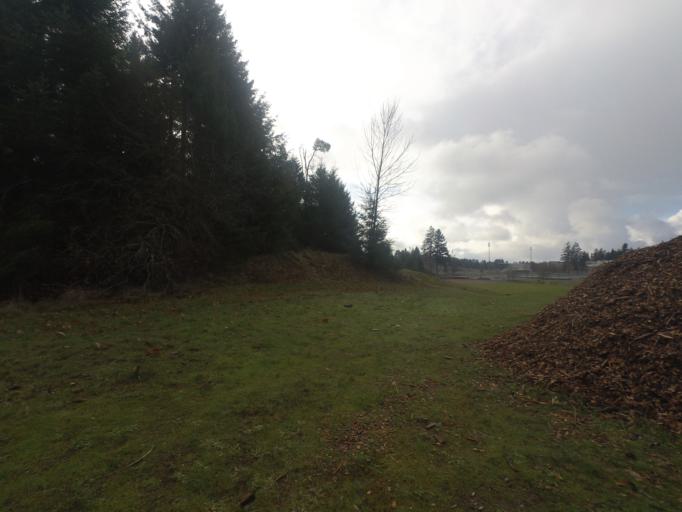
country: US
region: Washington
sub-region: Pierce County
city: University Place
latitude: 47.2244
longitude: -122.5481
